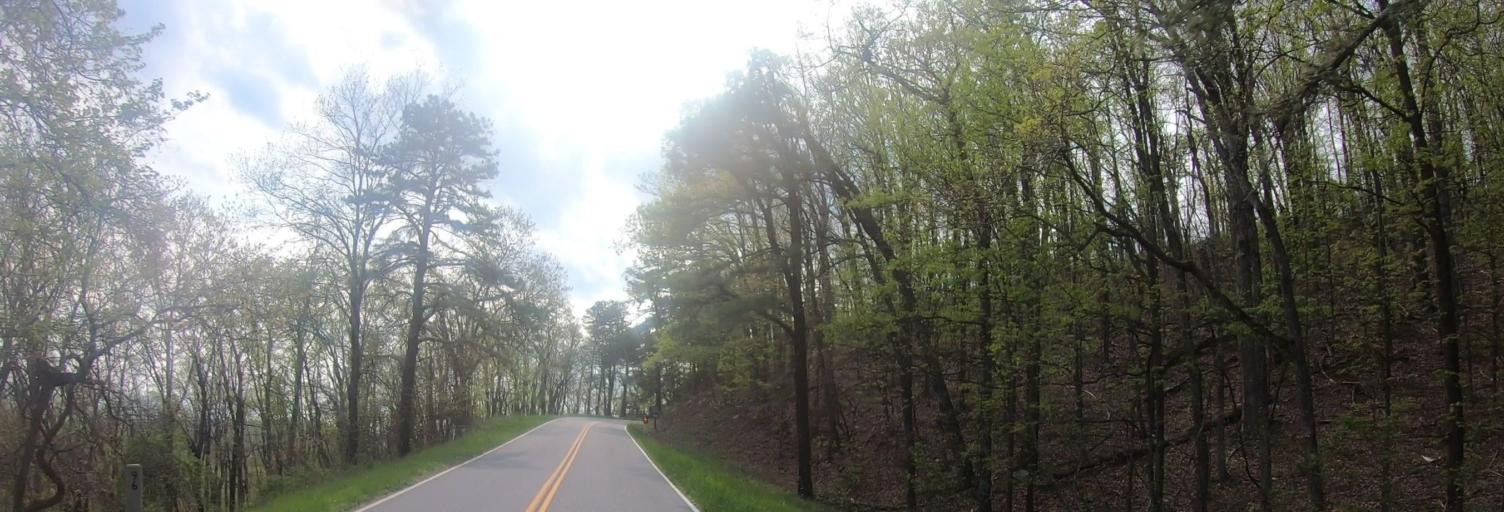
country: US
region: Virginia
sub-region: Augusta County
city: Dooms
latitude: 38.1059
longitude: -78.7815
